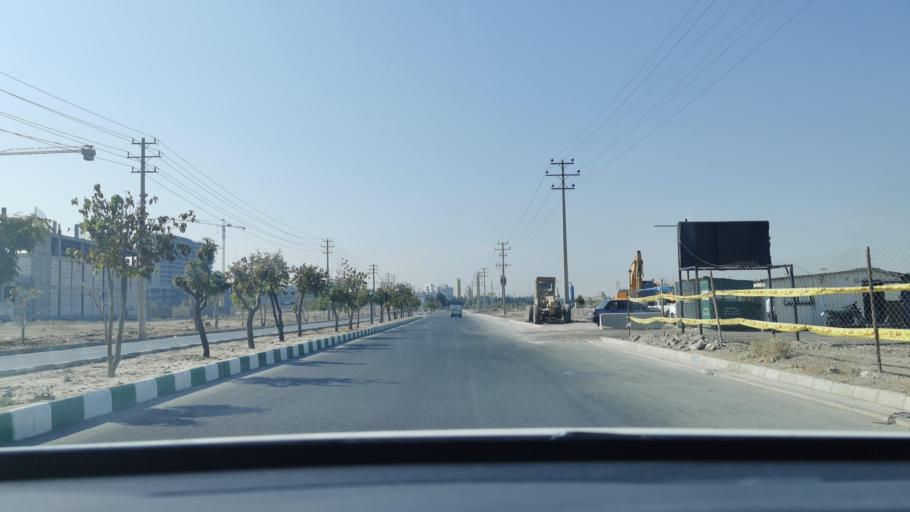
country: IR
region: Razavi Khorasan
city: Mashhad
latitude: 36.3480
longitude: 59.6087
